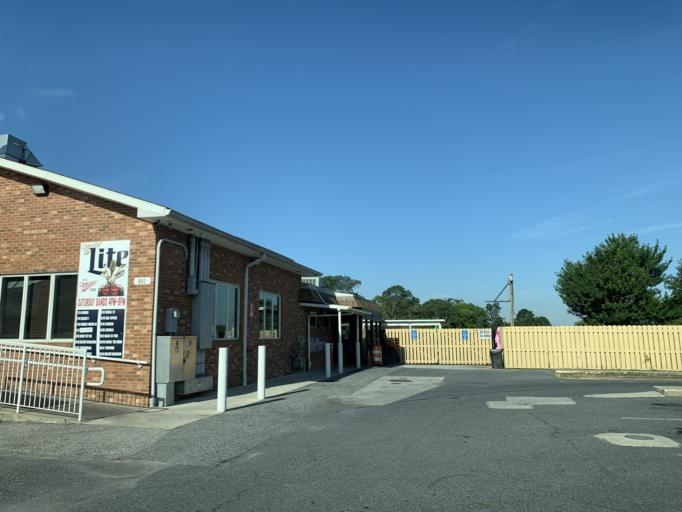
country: US
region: Maryland
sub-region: Baltimore County
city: Essex
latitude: 39.2962
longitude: -76.4634
